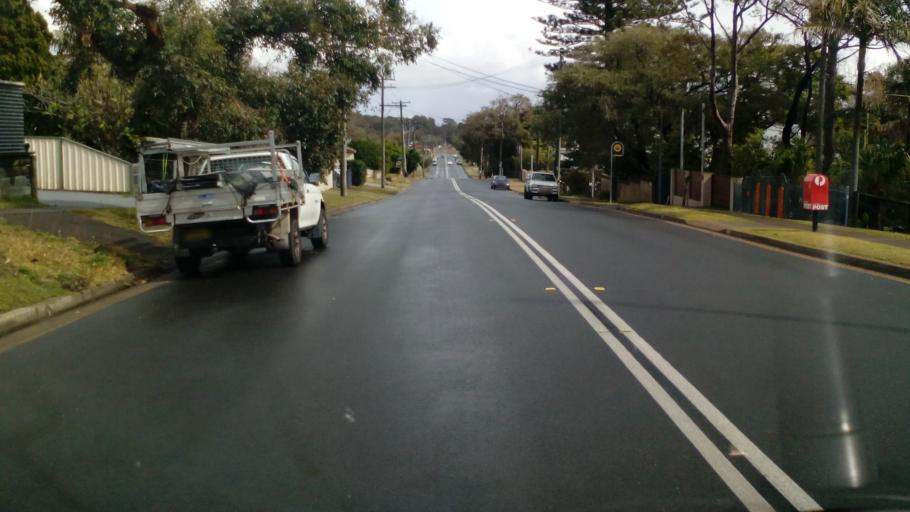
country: AU
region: New South Wales
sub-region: Lake Macquarie Shire
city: Belmont South
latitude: -33.0984
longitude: 151.6479
